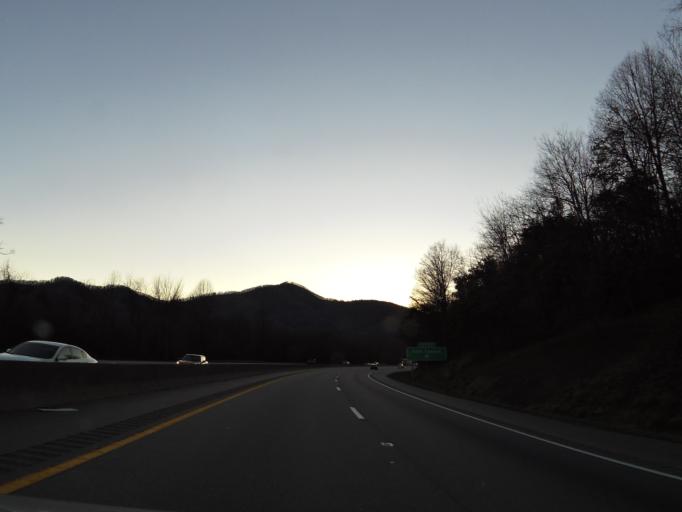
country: US
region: North Carolina
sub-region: Haywood County
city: Canton
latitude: 35.5438
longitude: -82.7478
